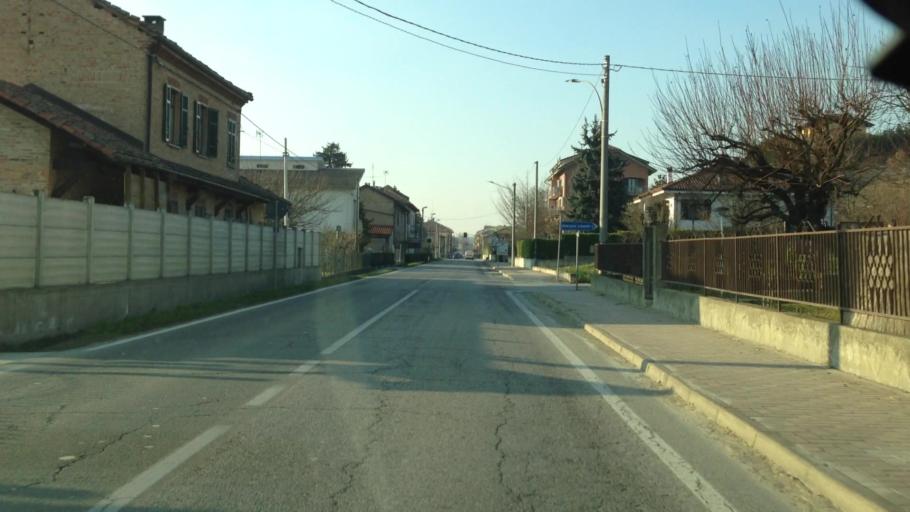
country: IT
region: Piedmont
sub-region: Provincia di Asti
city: Montegrosso
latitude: 44.8174
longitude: 8.2475
